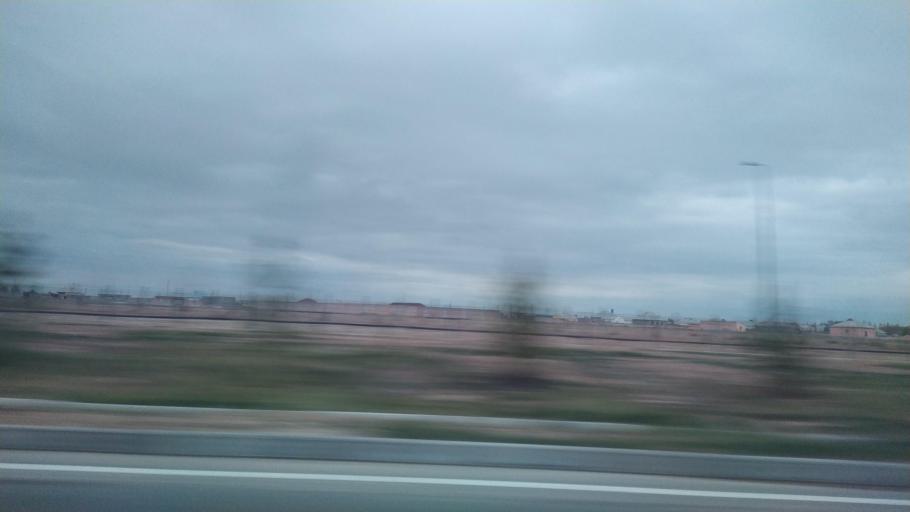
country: KZ
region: Ongtustik Qazaqstan
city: Turkestan
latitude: 43.2743
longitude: 68.4059
